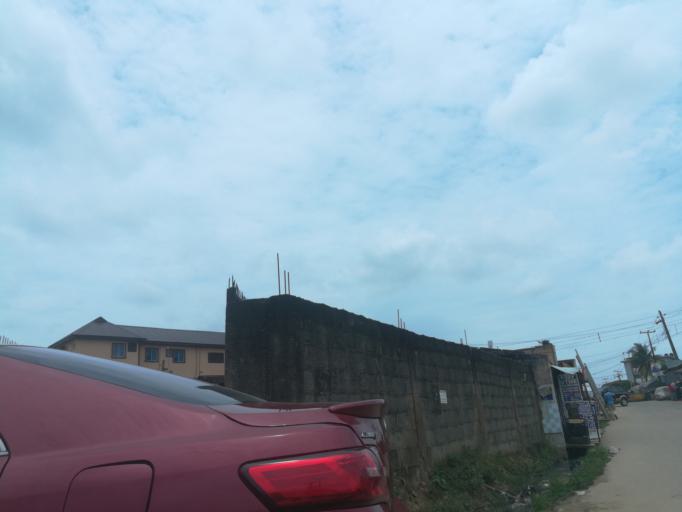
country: NG
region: Lagos
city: Somolu
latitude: 6.5241
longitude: 3.3842
